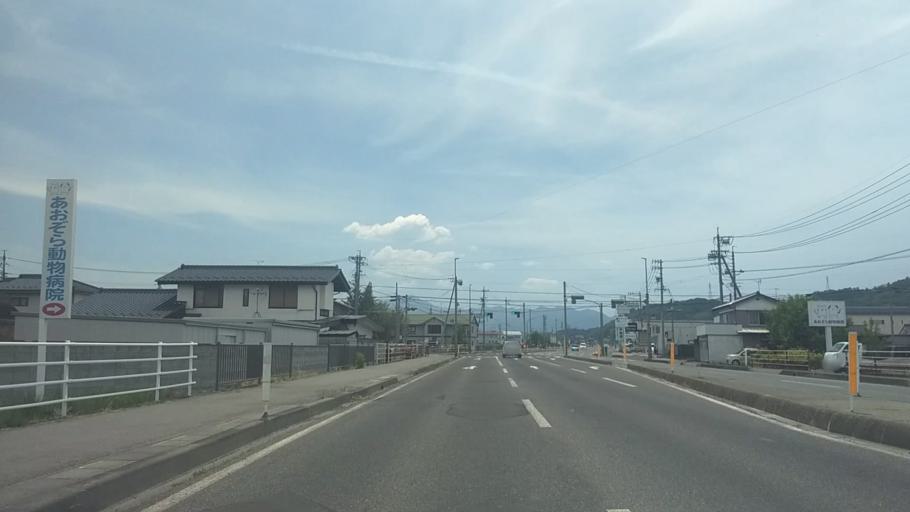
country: JP
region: Nagano
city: Saku
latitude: 36.2128
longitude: 138.4645
